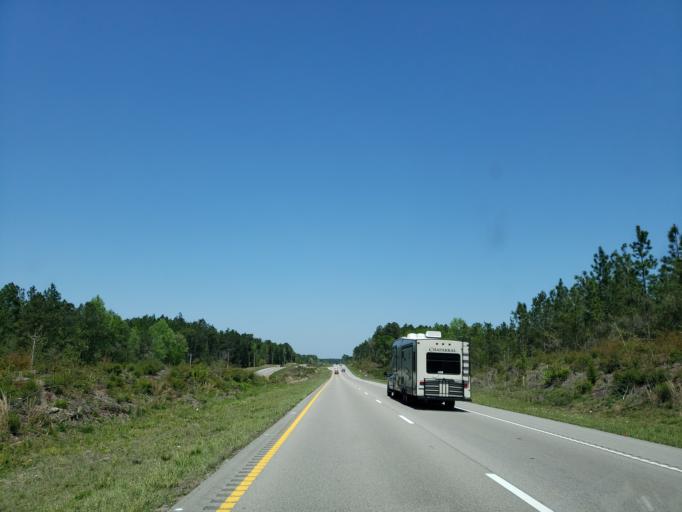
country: US
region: Mississippi
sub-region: Stone County
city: Wiggins
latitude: 30.9612
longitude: -89.1920
